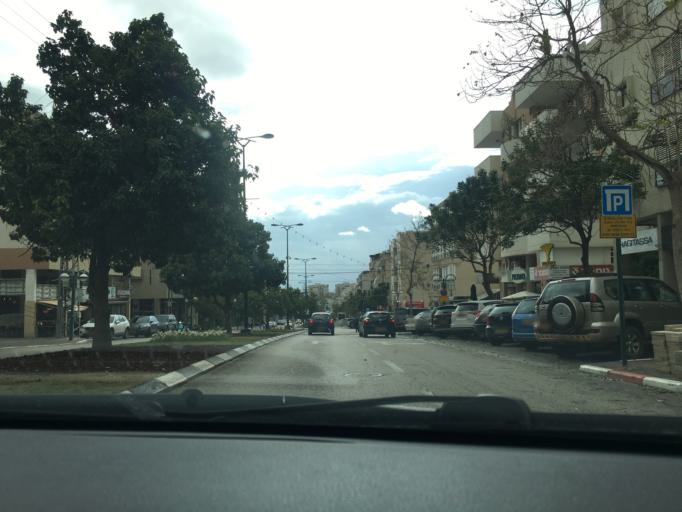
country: IL
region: Tel Aviv
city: Ramat HaSharon
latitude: 32.1431
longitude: 34.8436
